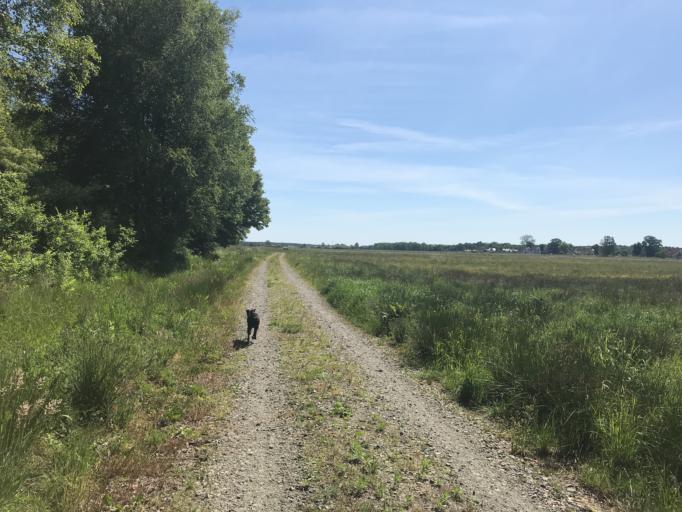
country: PL
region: West Pomeranian Voivodeship
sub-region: Powiat goleniowski
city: Goleniow
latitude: 53.5930
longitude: 14.7503
